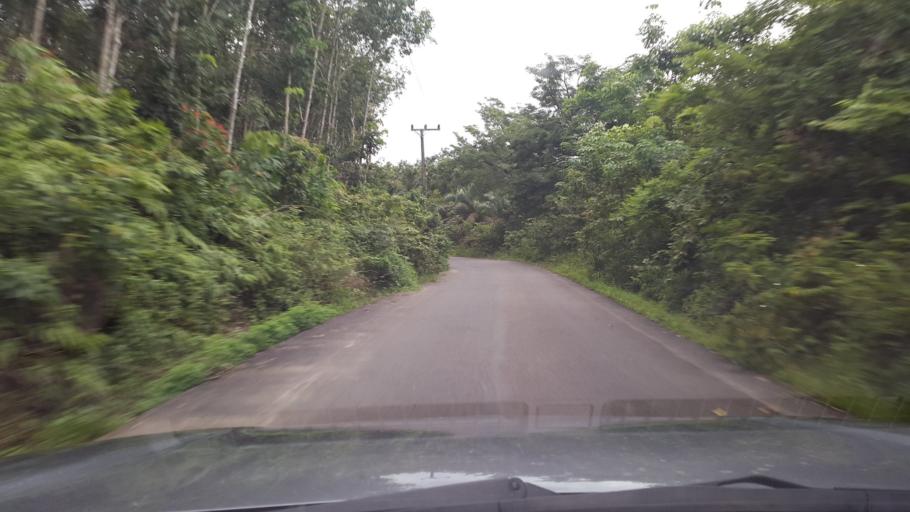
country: ID
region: South Sumatra
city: Gunungmenang
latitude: -3.1346
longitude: 103.9408
